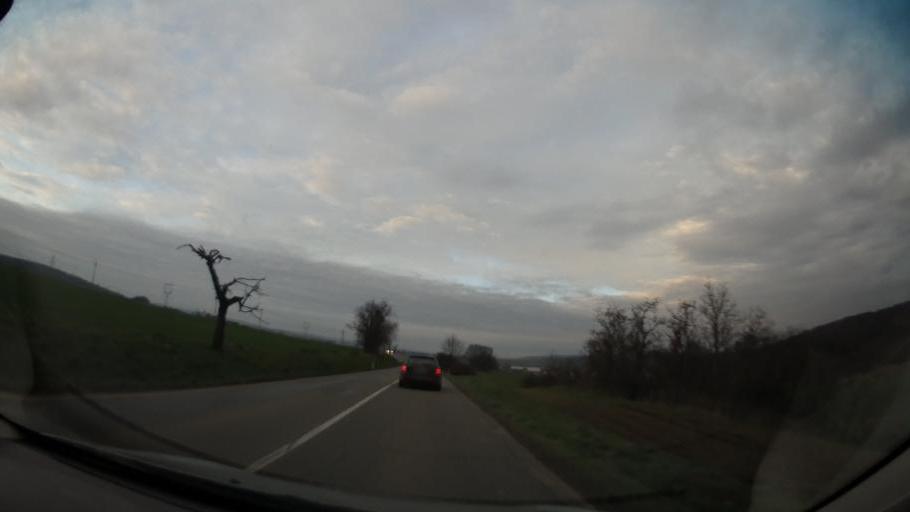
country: CZ
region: South Moravian
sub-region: Okres Brno-Venkov
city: Rosice
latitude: 49.1620
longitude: 16.3941
